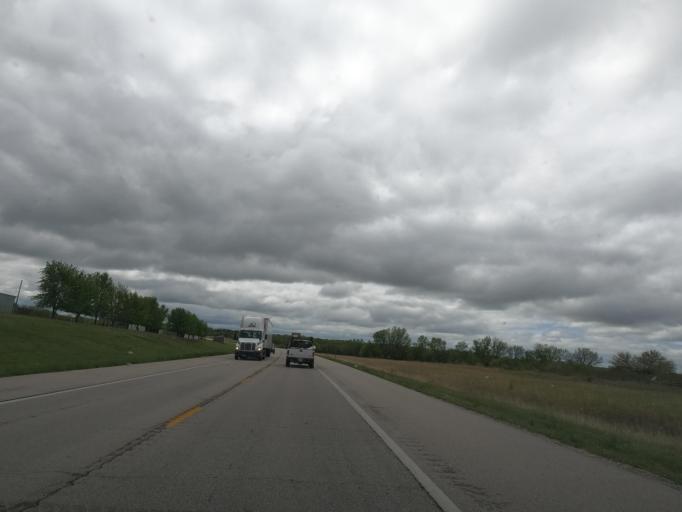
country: US
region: Kansas
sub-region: Wilson County
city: Fredonia
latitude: 37.5221
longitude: -95.8010
